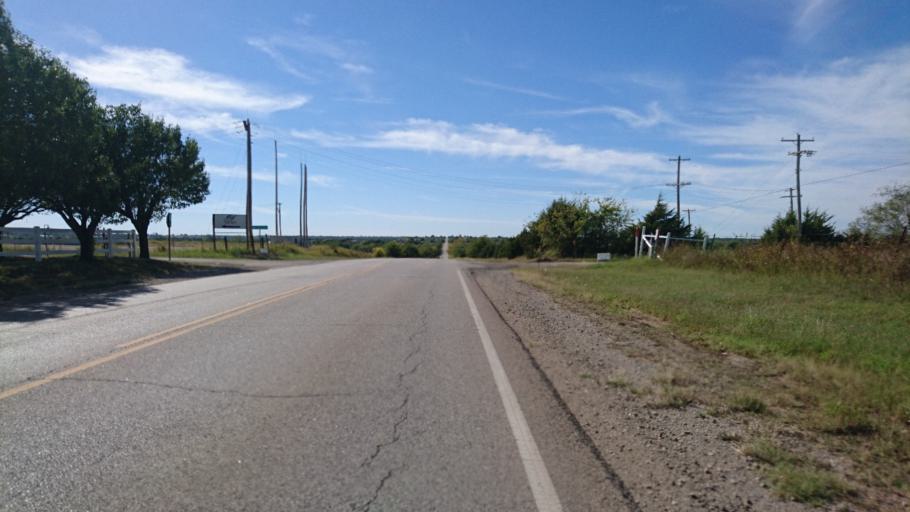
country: US
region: Oklahoma
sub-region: Lincoln County
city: Chandler
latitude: 35.7099
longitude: -96.7868
